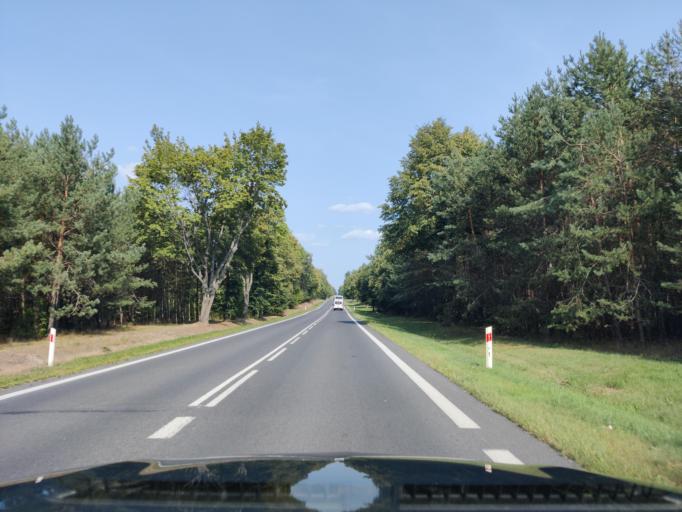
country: PL
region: Masovian Voivodeship
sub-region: Powiat makowski
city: Szelkow
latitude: 52.8373
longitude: 21.2495
